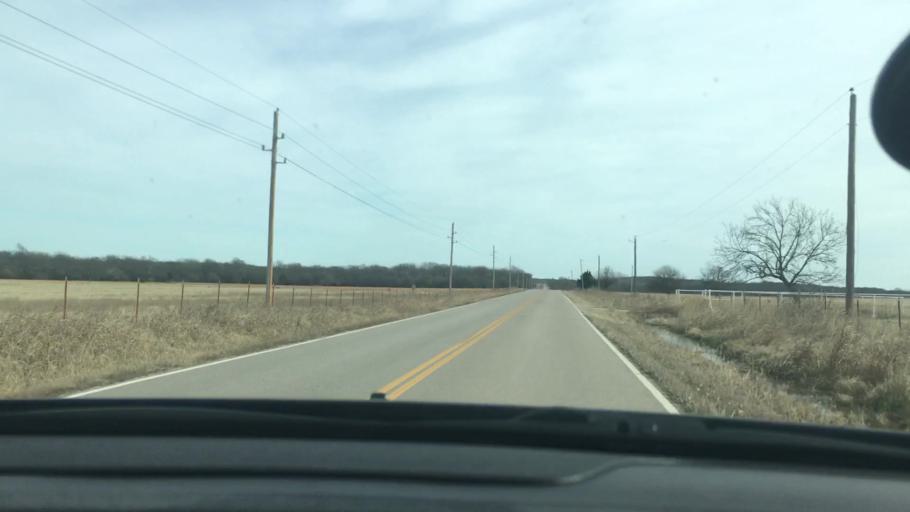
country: US
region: Oklahoma
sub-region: Murray County
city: Sulphur
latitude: 34.4049
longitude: -96.8750
